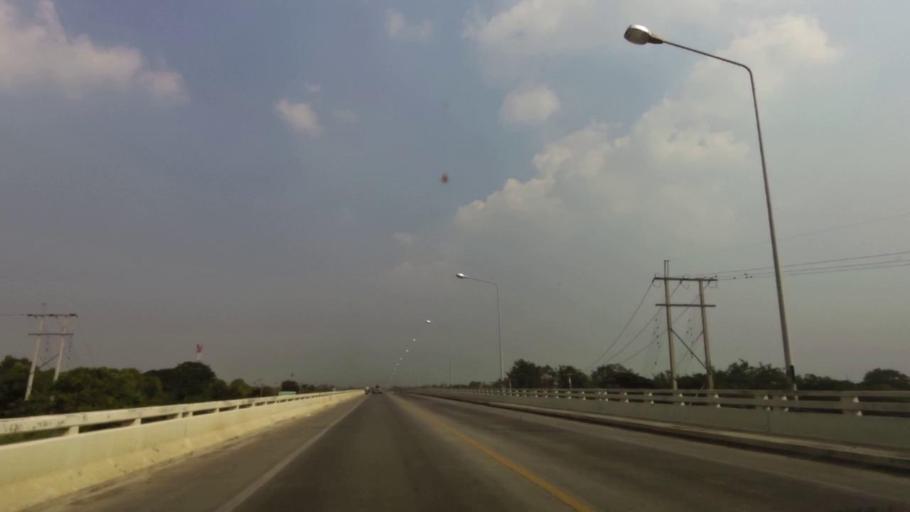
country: TH
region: Phra Nakhon Si Ayutthaya
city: Phra Nakhon Si Ayutthaya
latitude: 14.3049
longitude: 100.5672
